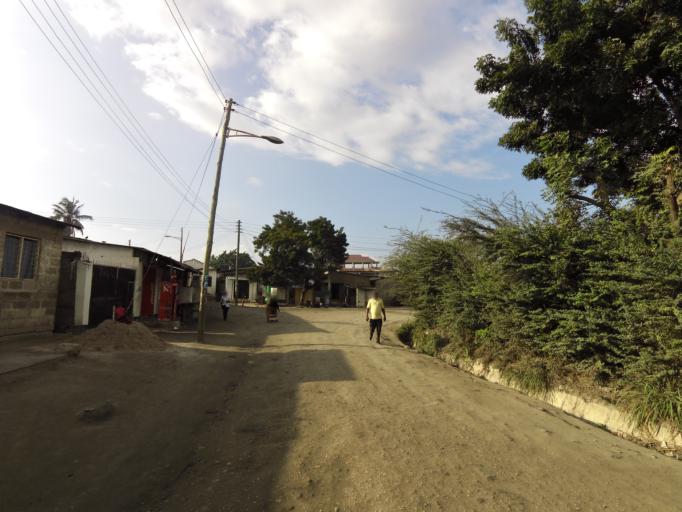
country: TZ
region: Dar es Salaam
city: Magomeni
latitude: -6.7910
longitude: 39.2305
